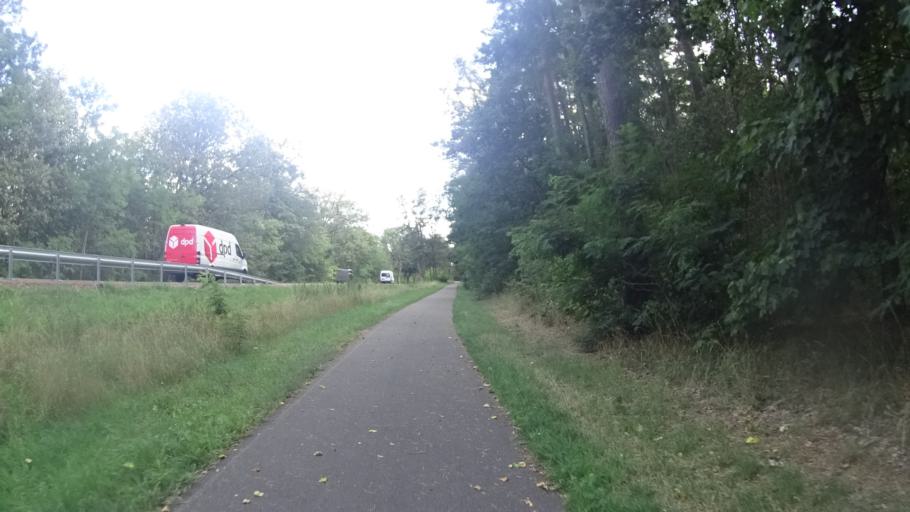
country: DE
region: Brandenburg
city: Rhinow
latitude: 52.7170
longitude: 12.3658
